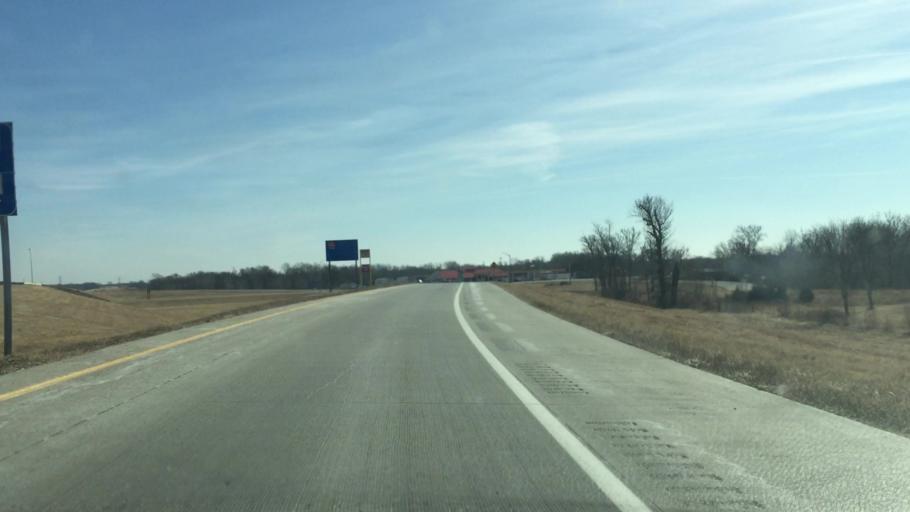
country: US
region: Kansas
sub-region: Labette County
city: Parsons
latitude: 37.3669
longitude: -95.2621
